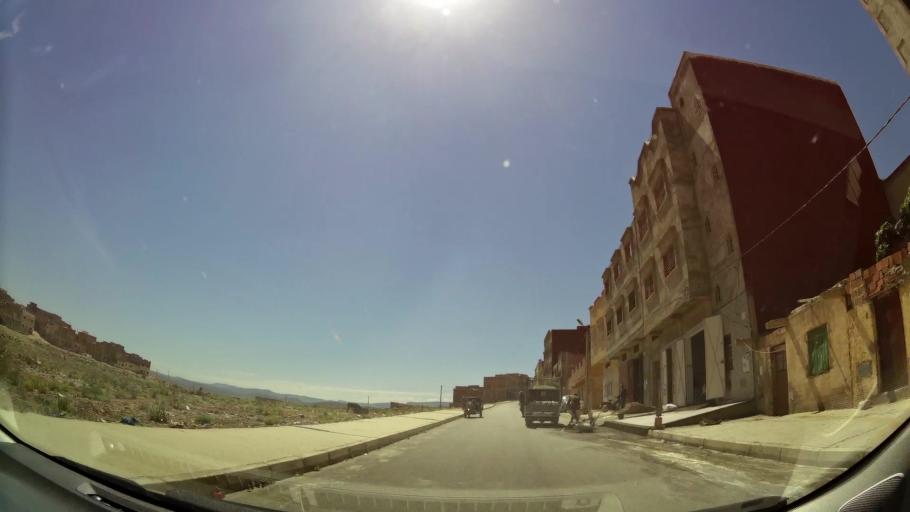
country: MA
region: Oriental
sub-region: Oujda-Angad
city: Oujda
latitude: 34.6506
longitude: -1.8741
